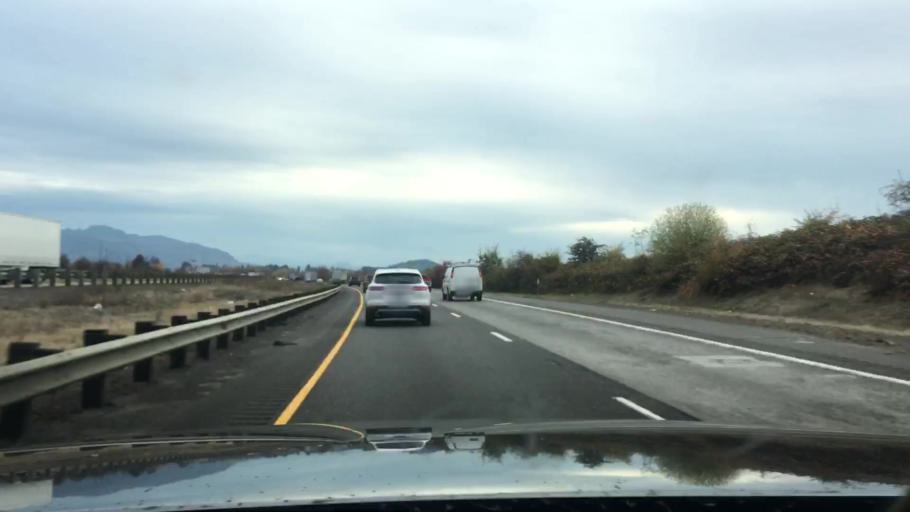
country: US
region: Oregon
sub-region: Lane County
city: Creswell
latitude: 43.9695
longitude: -123.0119
